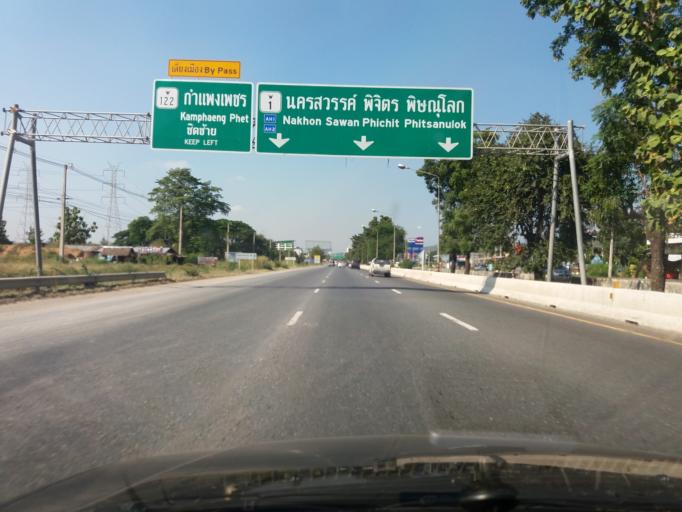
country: TH
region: Nakhon Sawan
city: Krok Phra
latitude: 15.6061
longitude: 100.1218
